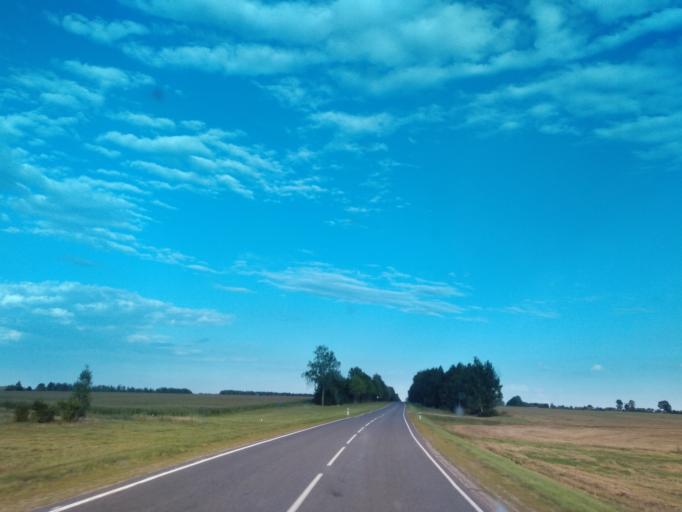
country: BY
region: Minsk
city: Uzda
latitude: 53.4373
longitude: 27.3303
